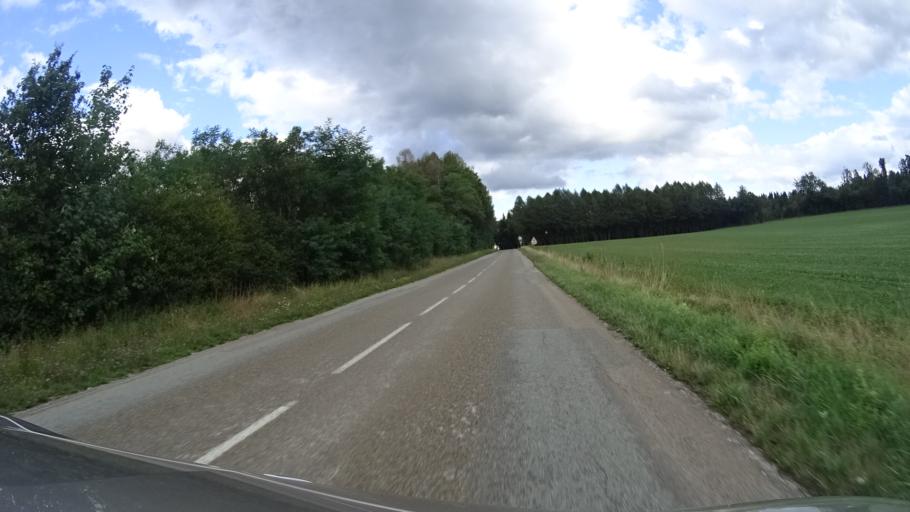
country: FR
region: Franche-Comte
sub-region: Departement du Doubs
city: Saone
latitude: 47.2237
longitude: 6.1419
